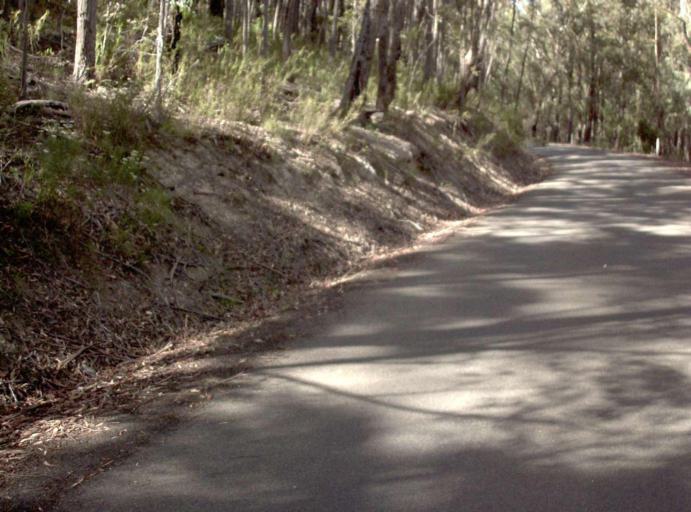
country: AU
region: Victoria
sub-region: East Gippsland
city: Lakes Entrance
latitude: -37.4469
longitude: 148.1276
